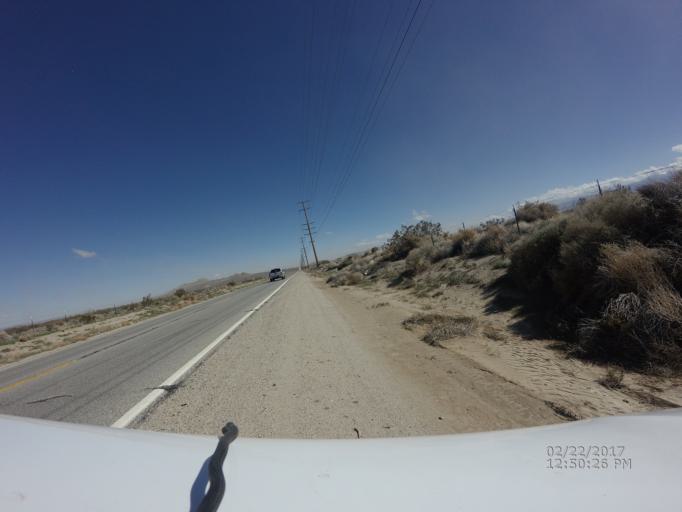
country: US
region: California
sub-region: Los Angeles County
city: Littlerock
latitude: 34.6166
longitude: -117.9491
